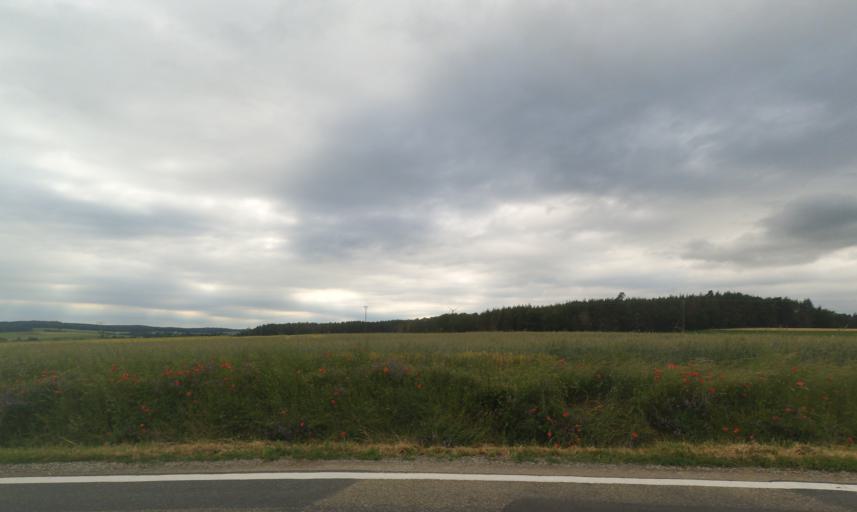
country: DE
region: Bavaria
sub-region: Regierungsbezirk Mittelfranken
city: Burghaslach
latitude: 49.7032
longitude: 10.5895
